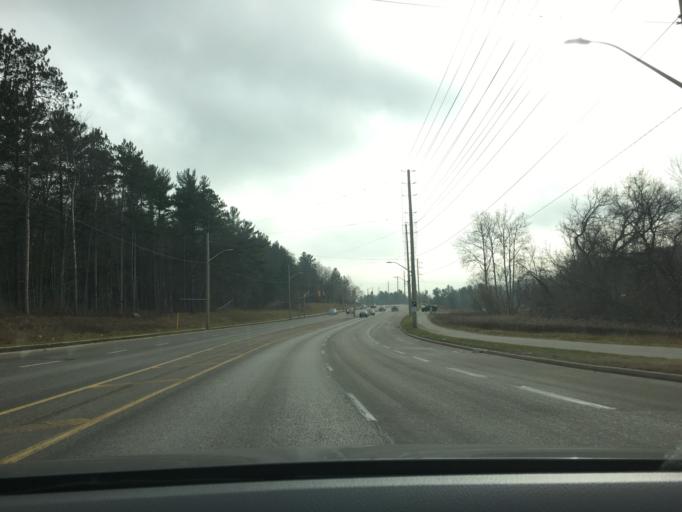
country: CA
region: Ontario
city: Barrie
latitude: 44.3876
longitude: -79.7302
